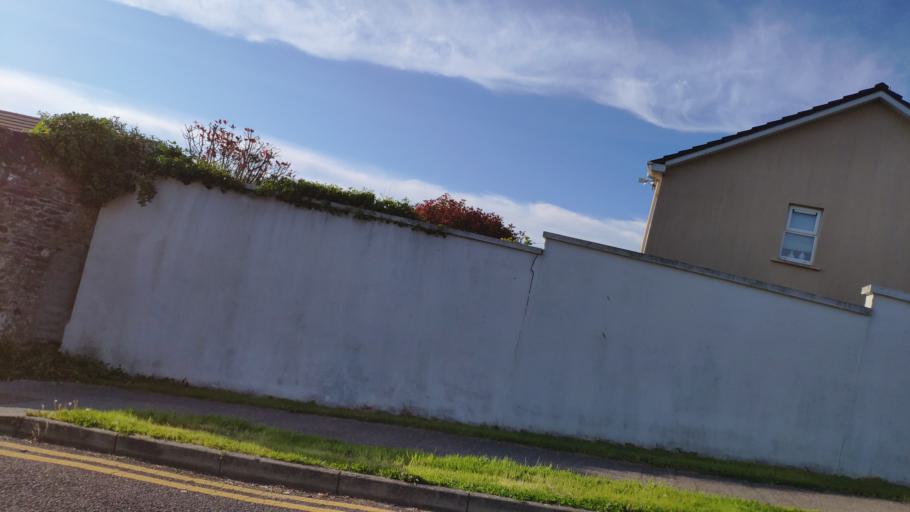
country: IE
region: Munster
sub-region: County Cork
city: Cork
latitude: 51.9081
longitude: -8.4710
